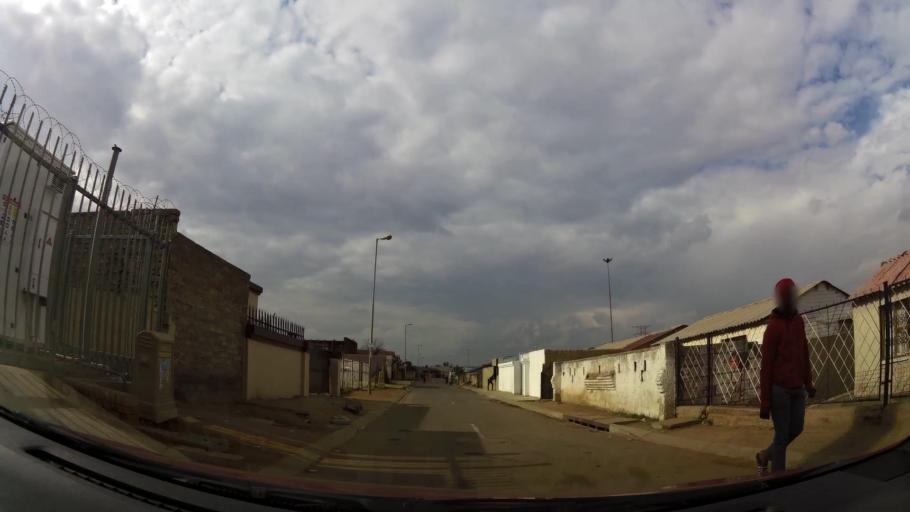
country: ZA
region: Gauteng
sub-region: City of Johannesburg Metropolitan Municipality
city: Soweto
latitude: -26.2372
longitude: 27.8650
